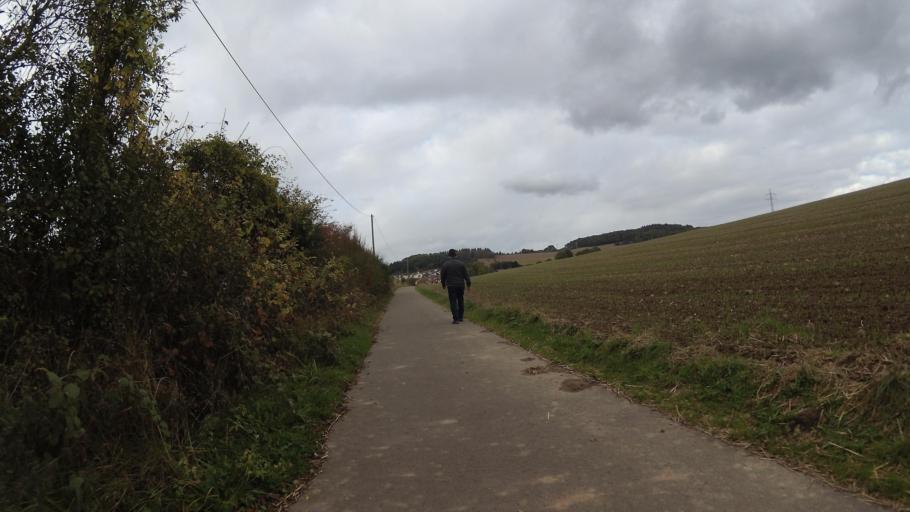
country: DE
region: Rheinland-Pfalz
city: Ohmbach
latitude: 49.4624
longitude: 7.3499
